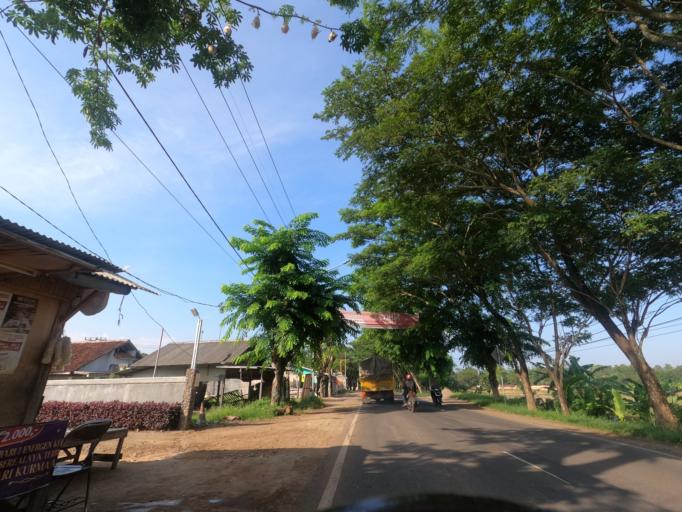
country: ID
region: West Java
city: Pamanukan
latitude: -6.5537
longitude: 107.8278
